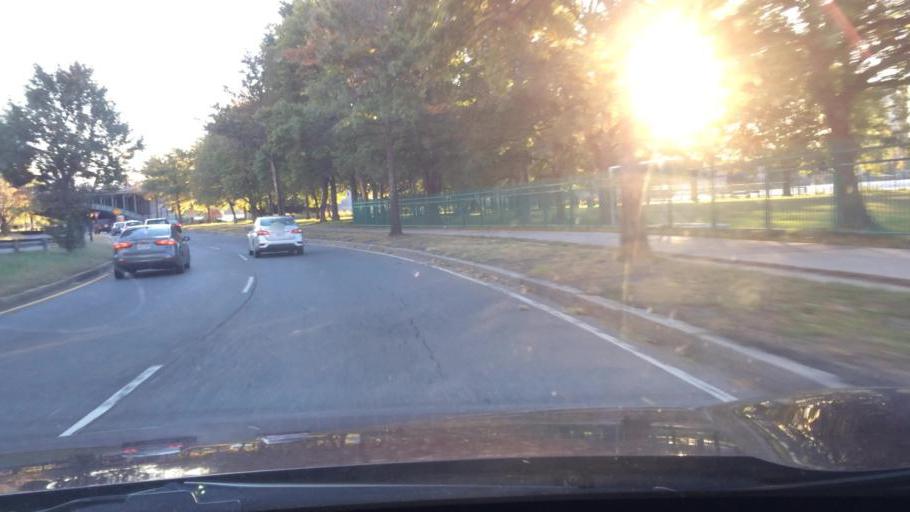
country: US
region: Massachusetts
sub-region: Suffolk County
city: Boston
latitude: 42.3628
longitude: -71.0723
